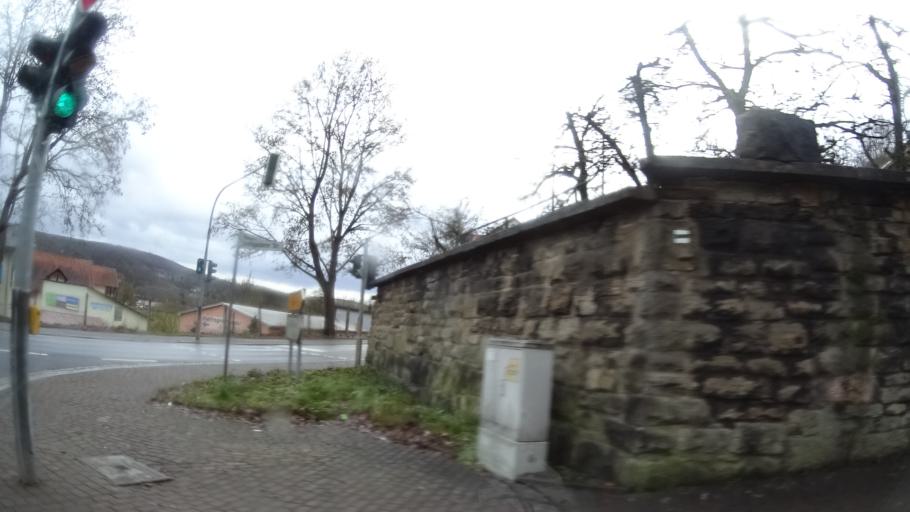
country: DE
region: Thuringia
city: Meiningen
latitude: 50.5610
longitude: 10.4078
